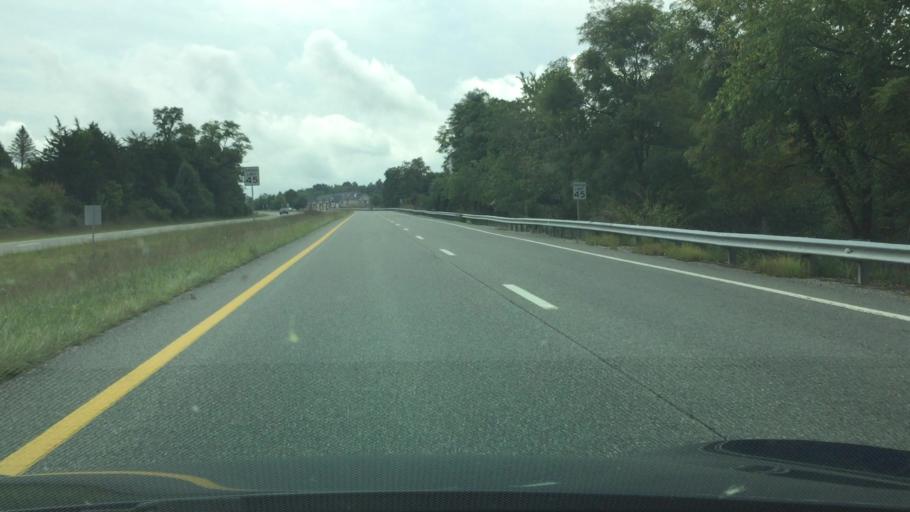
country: US
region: Virginia
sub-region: City of Radford
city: Radford
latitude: 37.1041
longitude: -80.5188
